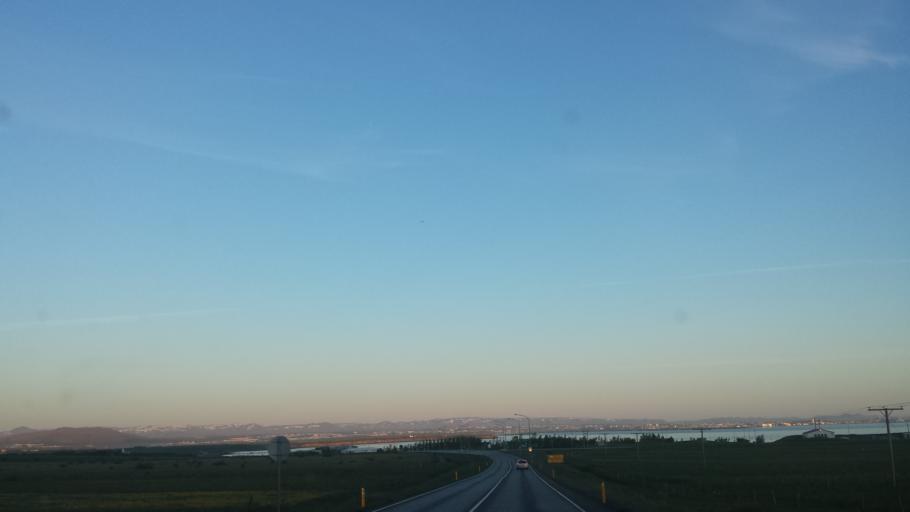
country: IS
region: Capital Region
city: Reykjavik
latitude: 64.2464
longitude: -21.8297
